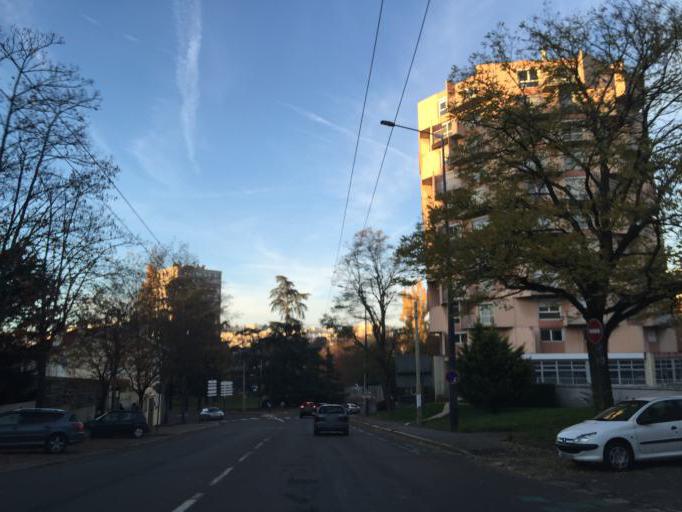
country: FR
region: Rhone-Alpes
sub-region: Departement de la Loire
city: Saint-Etienne
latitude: 45.4193
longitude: 4.4115
